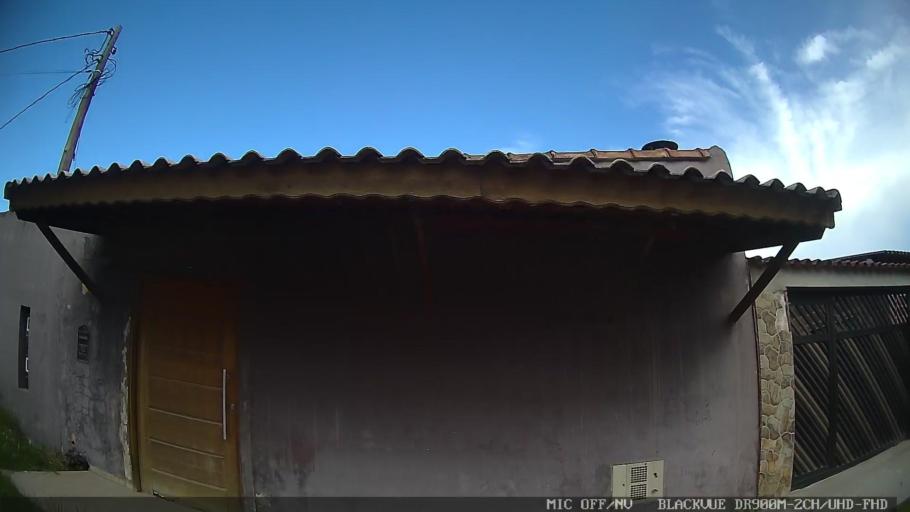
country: BR
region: Sao Paulo
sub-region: Iguape
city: Iguape
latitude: -24.7011
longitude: -47.5569
